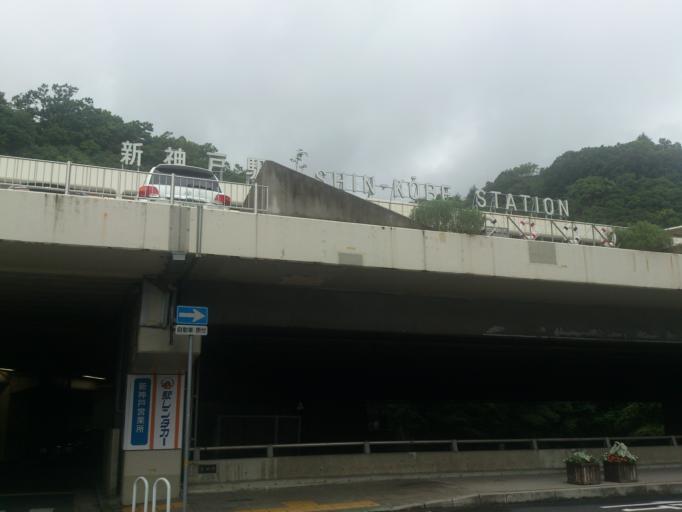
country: JP
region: Hyogo
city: Kobe
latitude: 34.7060
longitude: 135.1960
